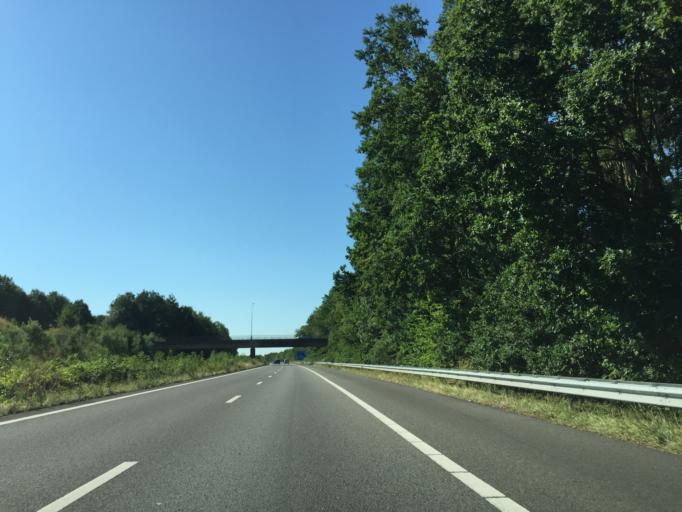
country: NL
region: Limburg
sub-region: Gemeente Maastricht
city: Heer
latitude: 50.8282
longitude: 5.7182
